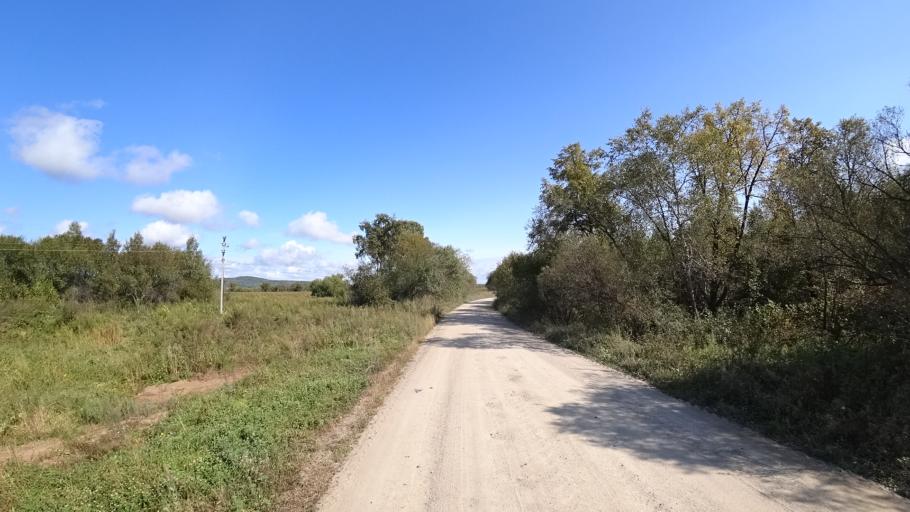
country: RU
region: Amur
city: Arkhara
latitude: 49.4100
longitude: 130.1630
